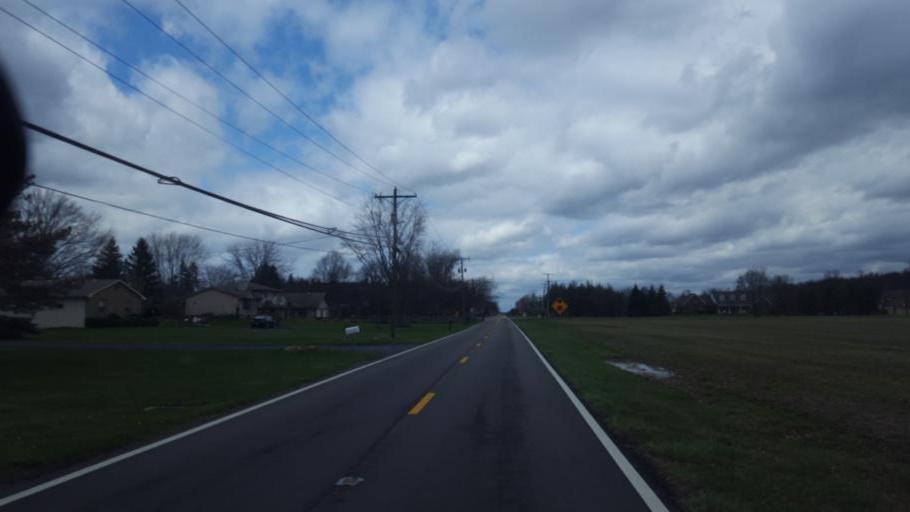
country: US
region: Ohio
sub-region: Franklin County
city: New Albany
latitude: 40.1281
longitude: -82.8583
